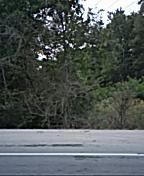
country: US
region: Kentucky
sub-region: Jefferson County
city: Douglass Hills
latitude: 38.2440
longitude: -85.5475
